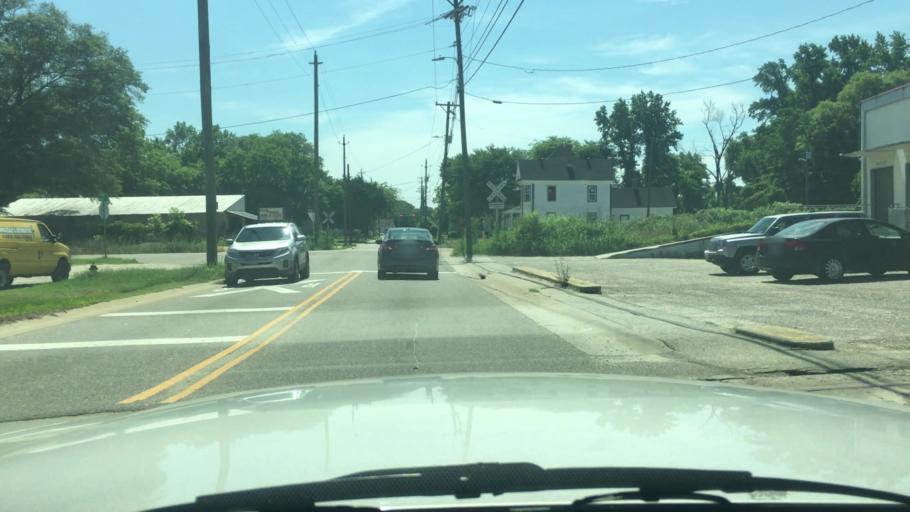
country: US
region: North Carolina
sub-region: Cumberland County
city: Fayetteville
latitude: 35.0469
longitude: -78.8832
